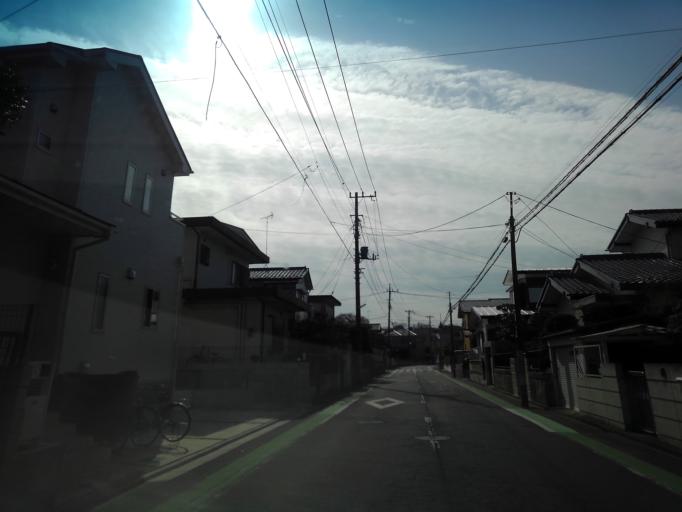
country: JP
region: Saitama
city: Tokorozawa
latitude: 35.7873
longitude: 139.5125
